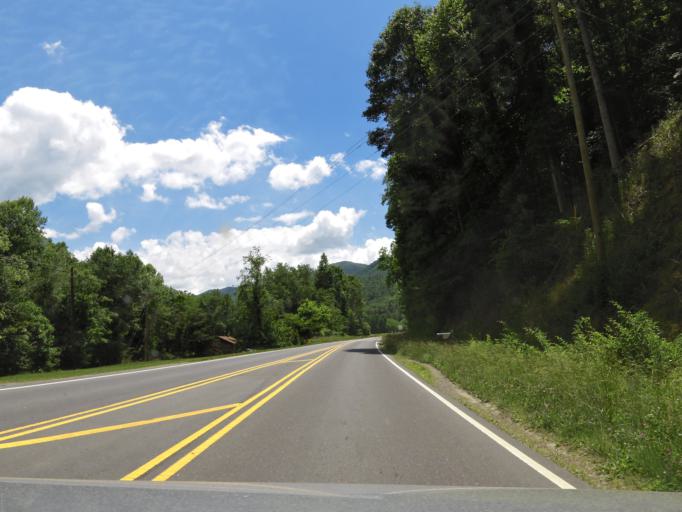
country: US
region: North Carolina
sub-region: Graham County
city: Robbinsville
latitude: 35.3069
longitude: -83.7947
